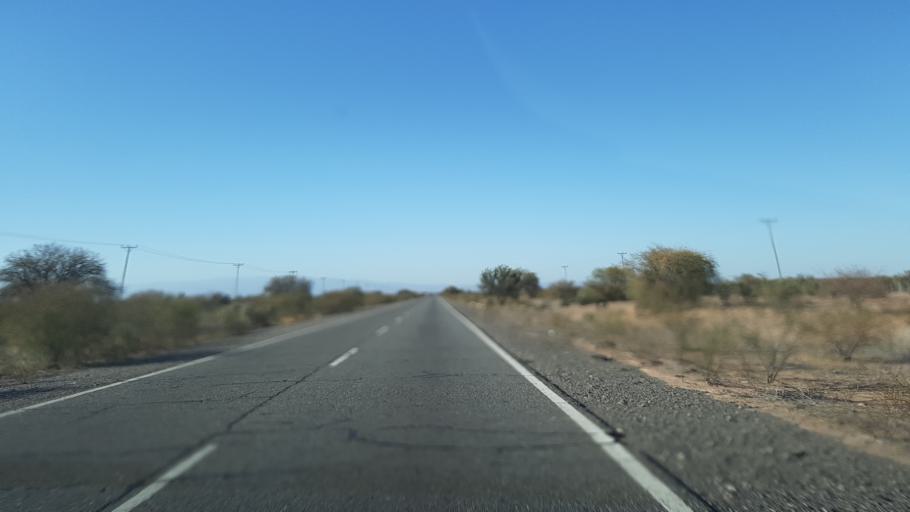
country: AR
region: San Juan
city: Caucete
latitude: -31.6436
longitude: -67.7575
